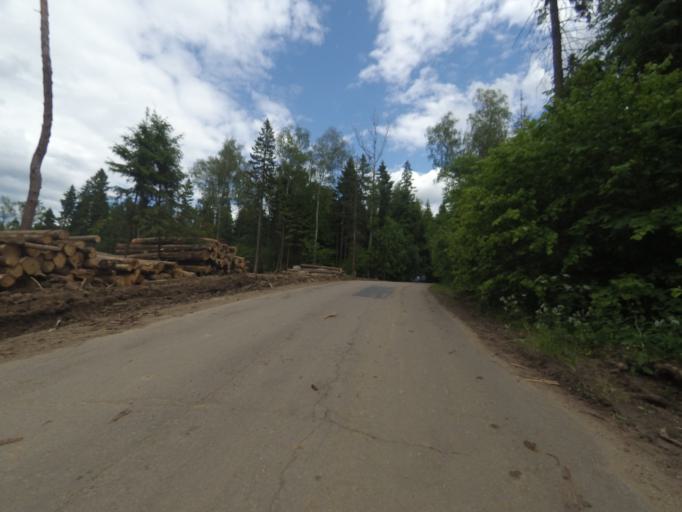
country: RU
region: Moskovskaya
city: Marfino
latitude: 56.0506
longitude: 37.6210
